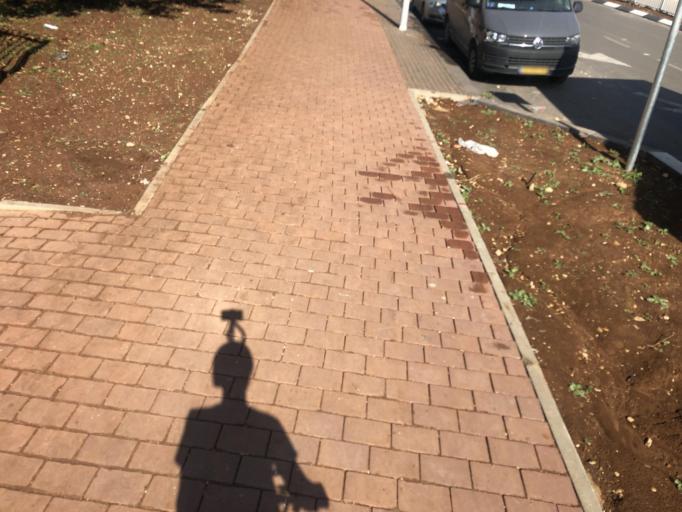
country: IL
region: Jerusalem
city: Modiin Ilit
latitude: 31.9262
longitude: 35.0463
